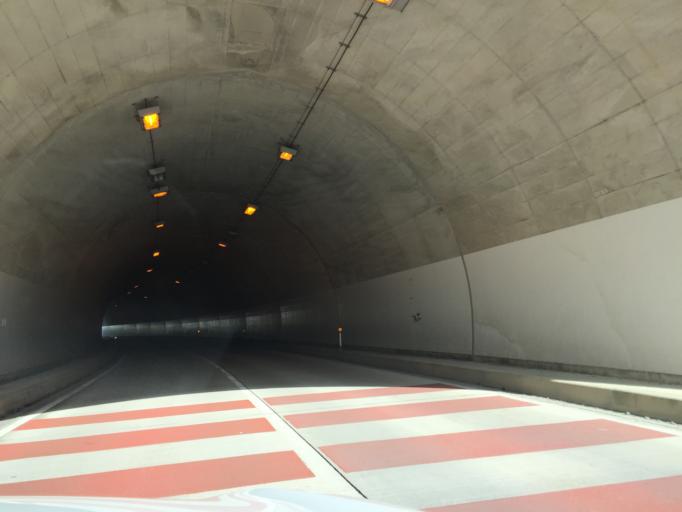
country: JP
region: Fukushima
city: Namie
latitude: 37.3617
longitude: 140.9522
